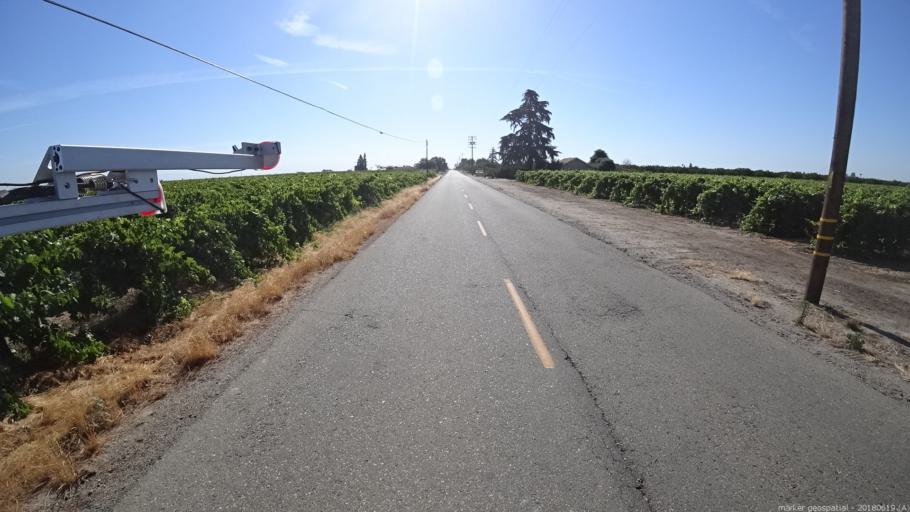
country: US
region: California
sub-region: Fresno County
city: Biola
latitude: 36.8296
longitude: -120.0732
